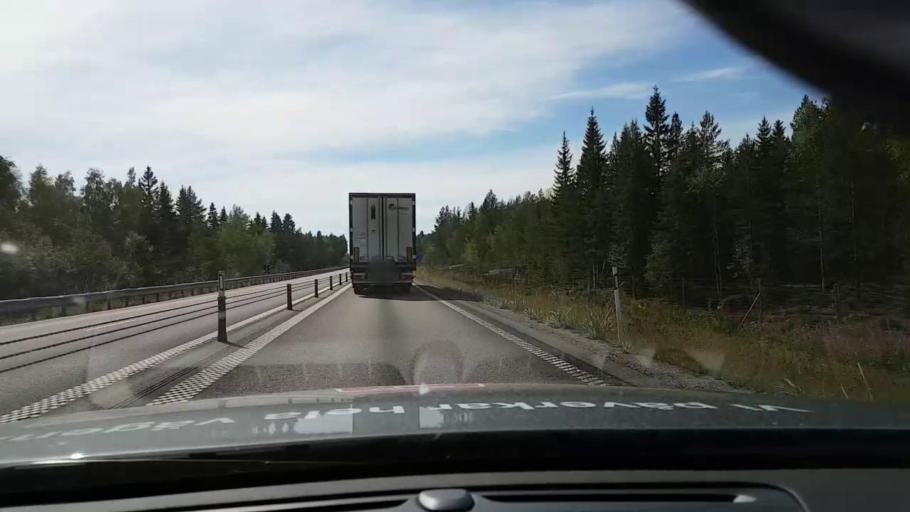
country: SE
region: Vaesternorrland
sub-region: OErnskoeldsviks Kommun
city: Husum
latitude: 63.4708
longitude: 19.2802
